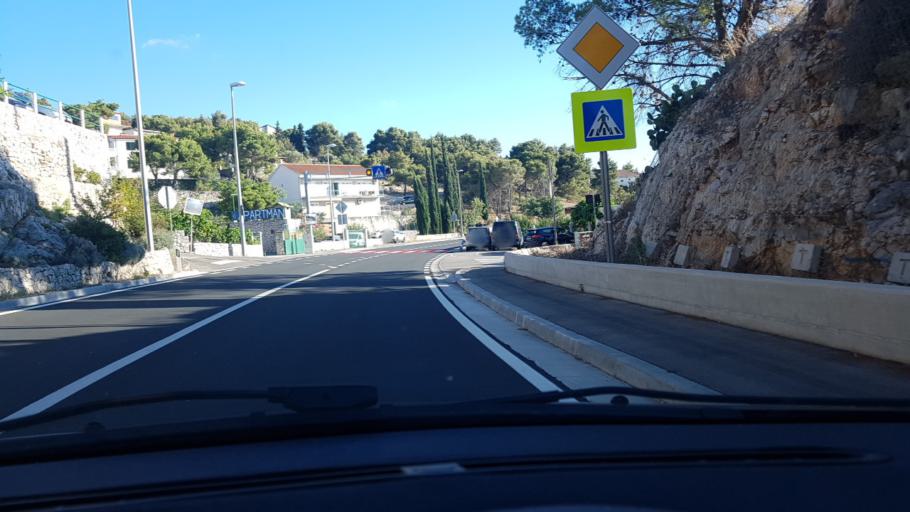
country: HR
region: Sibensko-Kniniska
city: Primosten
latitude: 43.5940
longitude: 15.9263
